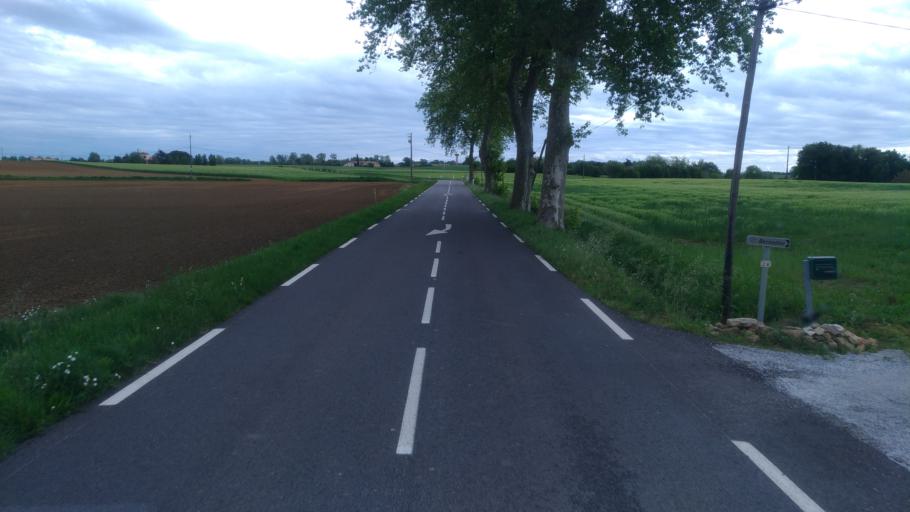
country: FR
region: Midi-Pyrenees
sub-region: Departement de la Haute-Garonne
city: Villefranche-de-Lauragais
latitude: 43.4262
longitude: 1.7608
